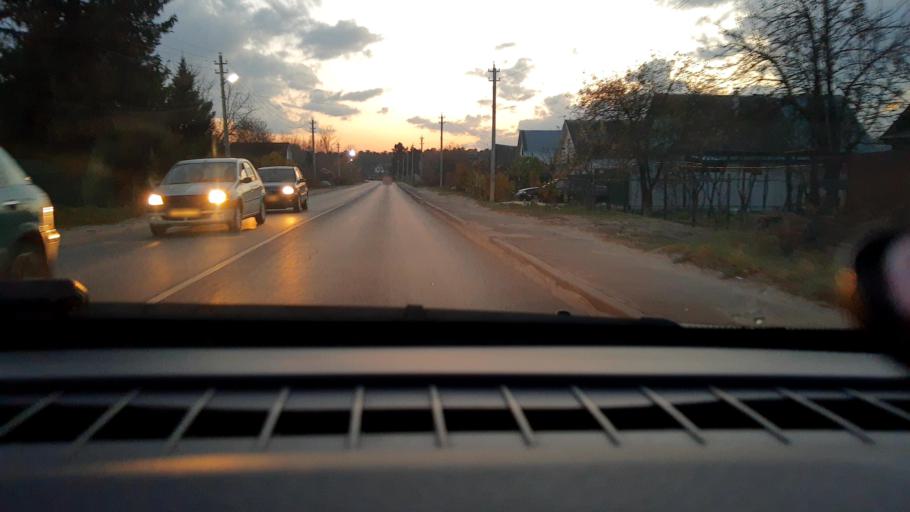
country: RU
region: Nizjnij Novgorod
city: Novaya Balakhna
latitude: 56.4848
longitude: 43.5743
